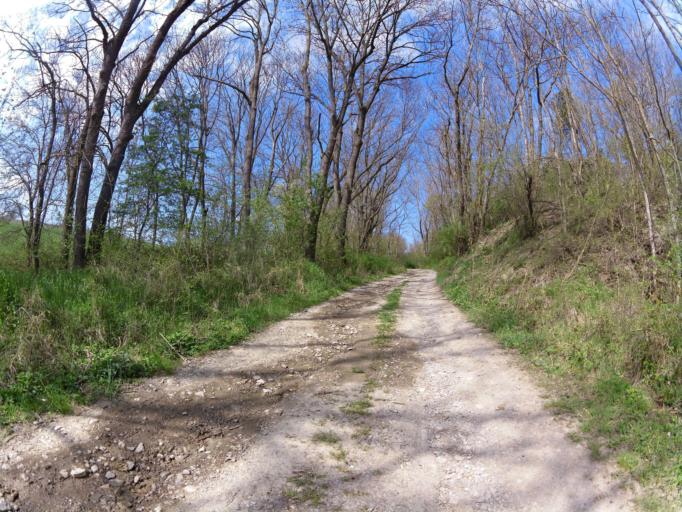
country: DE
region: Bavaria
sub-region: Regierungsbezirk Unterfranken
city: Winterhausen
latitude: 49.6756
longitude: 10.0060
